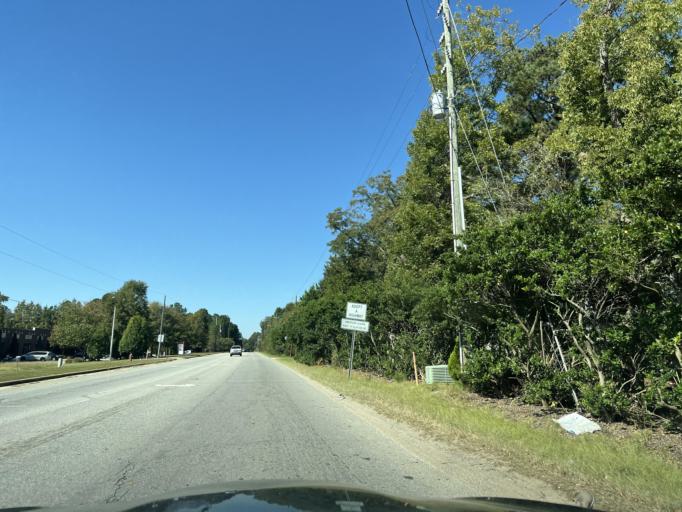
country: US
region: North Carolina
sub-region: Johnston County
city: Clayton
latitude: 35.6691
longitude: -78.4769
